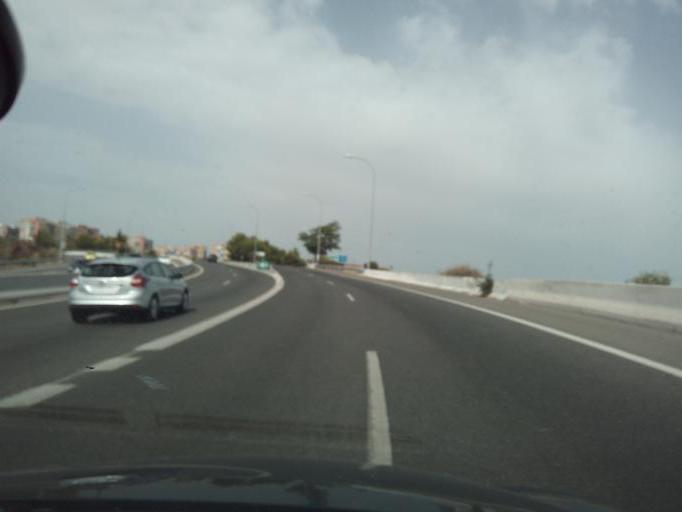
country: ES
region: Madrid
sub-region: Provincia de Madrid
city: Hortaleza
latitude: 40.4802
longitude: -3.6372
